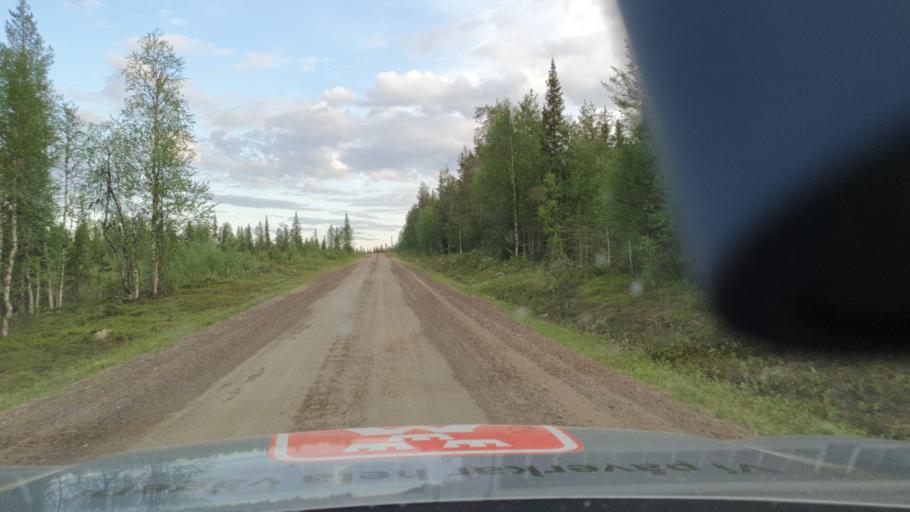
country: SE
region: Norrbotten
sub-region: Bodens Kommun
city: Boden
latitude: 66.5678
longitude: 21.4295
